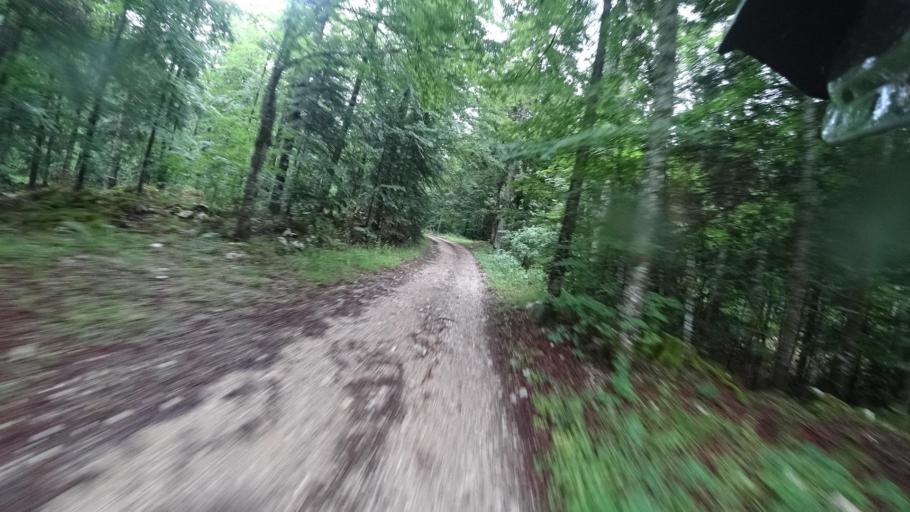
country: HR
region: Karlovacka
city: Plaski
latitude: 44.9294
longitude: 15.4266
